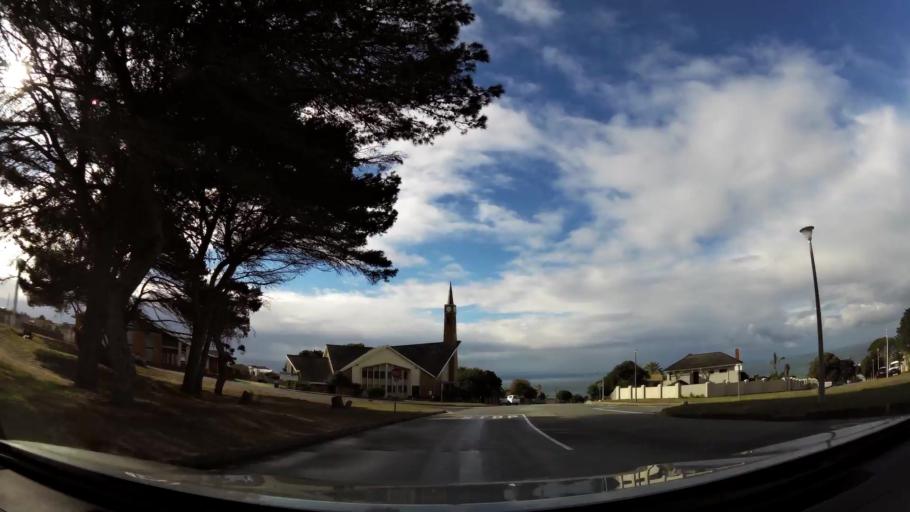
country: ZA
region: Western Cape
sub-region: Eden District Municipality
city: Mossel Bay
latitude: -34.1857
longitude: 22.1329
